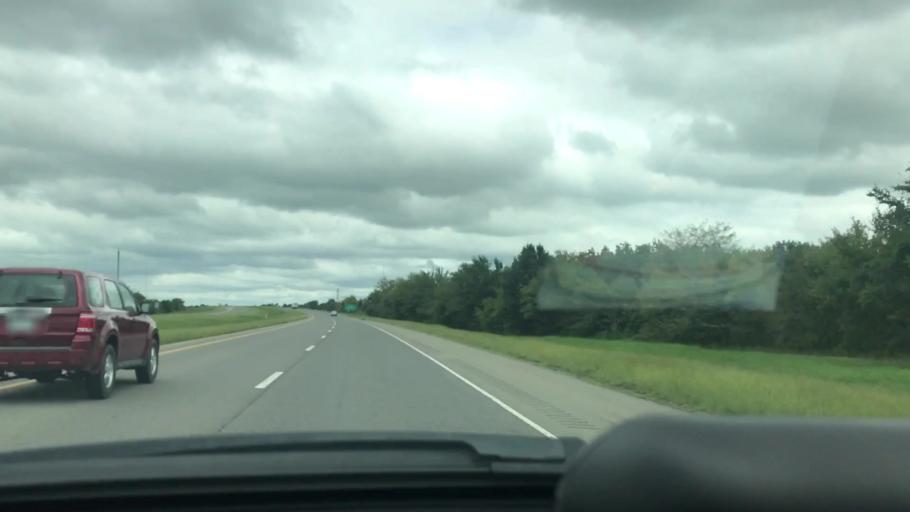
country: US
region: Oklahoma
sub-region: McIntosh County
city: Checotah
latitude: 35.5661
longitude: -95.4918
